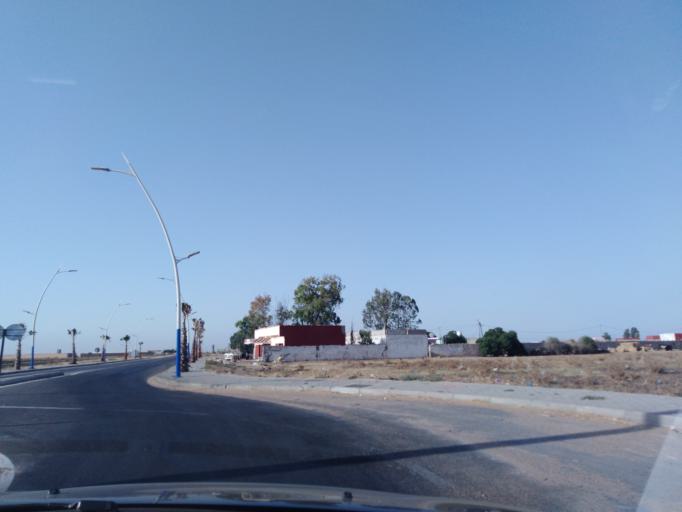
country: MA
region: Doukkala-Abda
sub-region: El-Jadida
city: Sidi Bennour
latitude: 32.5878
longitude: -8.7102
